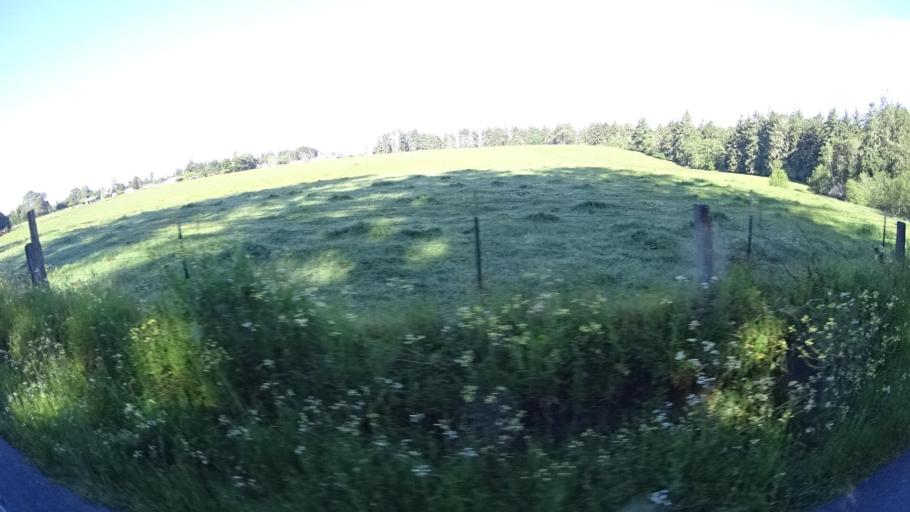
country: US
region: California
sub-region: Humboldt County
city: McKinleyville
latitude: 40.9947
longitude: -124.1005
